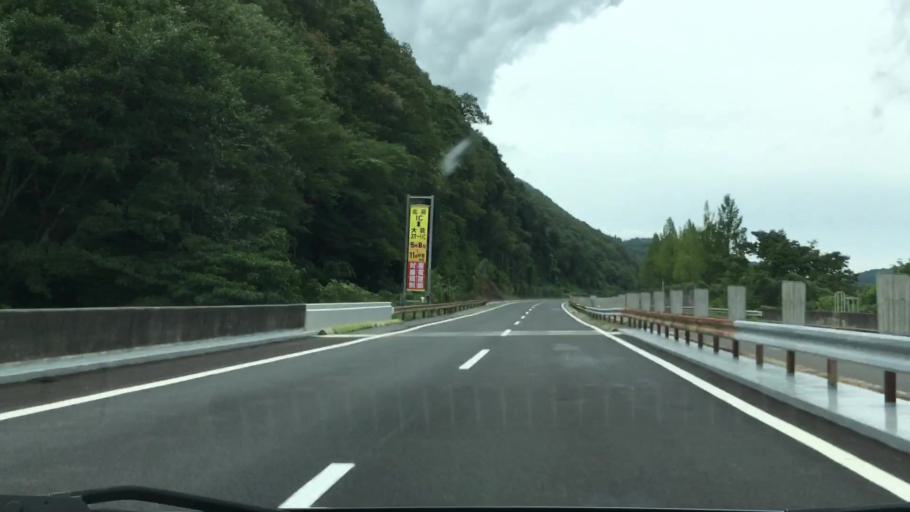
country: JP
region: Okayama
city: Niimi
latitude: 34.9719
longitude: 133.6245
